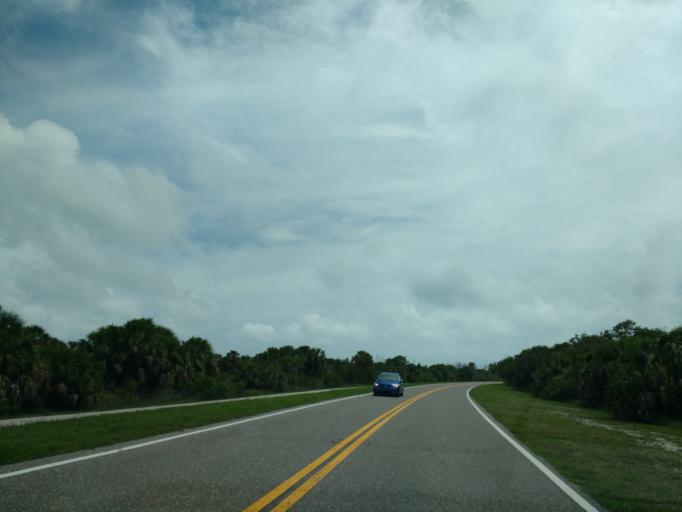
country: US
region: Florida
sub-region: Pinellas County
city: Tierra Verde
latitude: 27.6310
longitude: -82.7025
